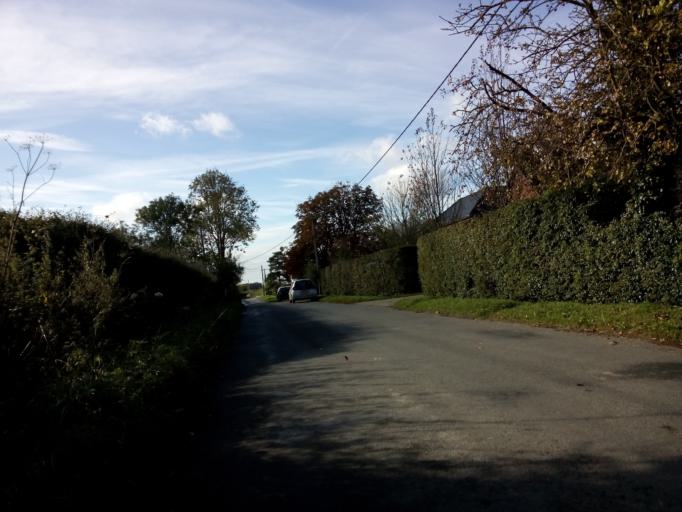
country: GB
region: England
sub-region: Suffolk
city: Capel Saint Mary
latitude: 52.0374
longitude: 1.0417
